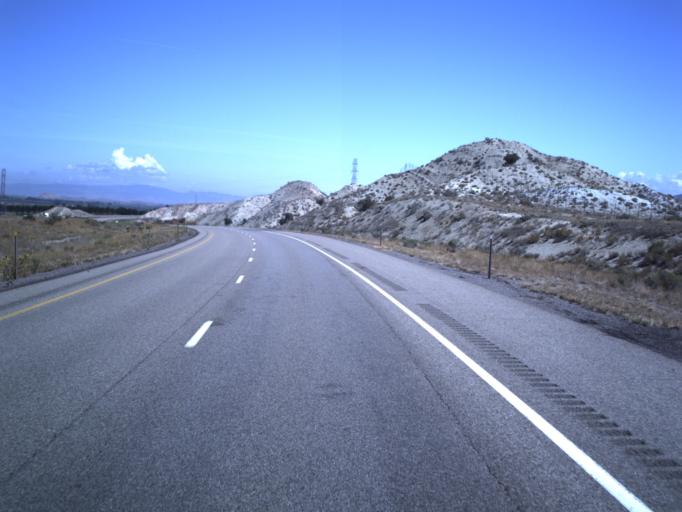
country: US
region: Utah
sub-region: Sevier County
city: Aurora
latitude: 38.8924
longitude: -111.9060
